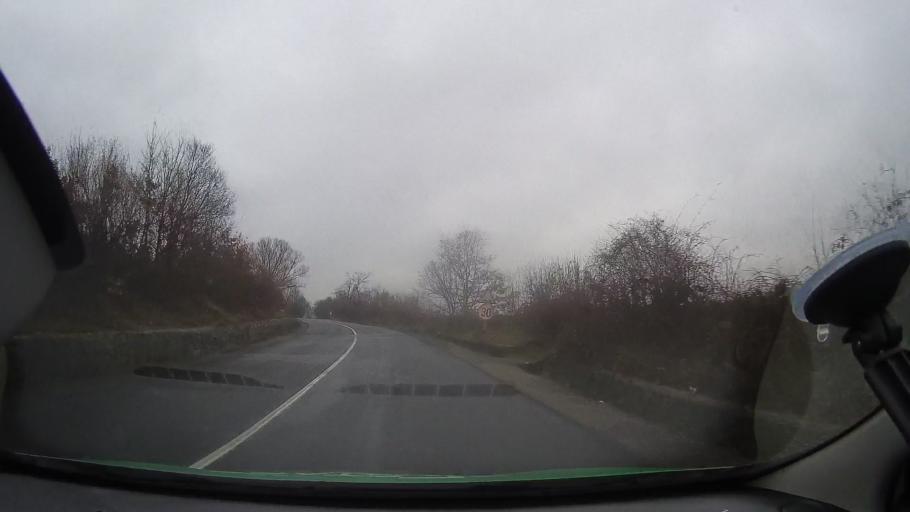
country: RO
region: Arad
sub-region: Comuna Varfurile
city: Varfurile
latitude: 46.3274
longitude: 22.4920
